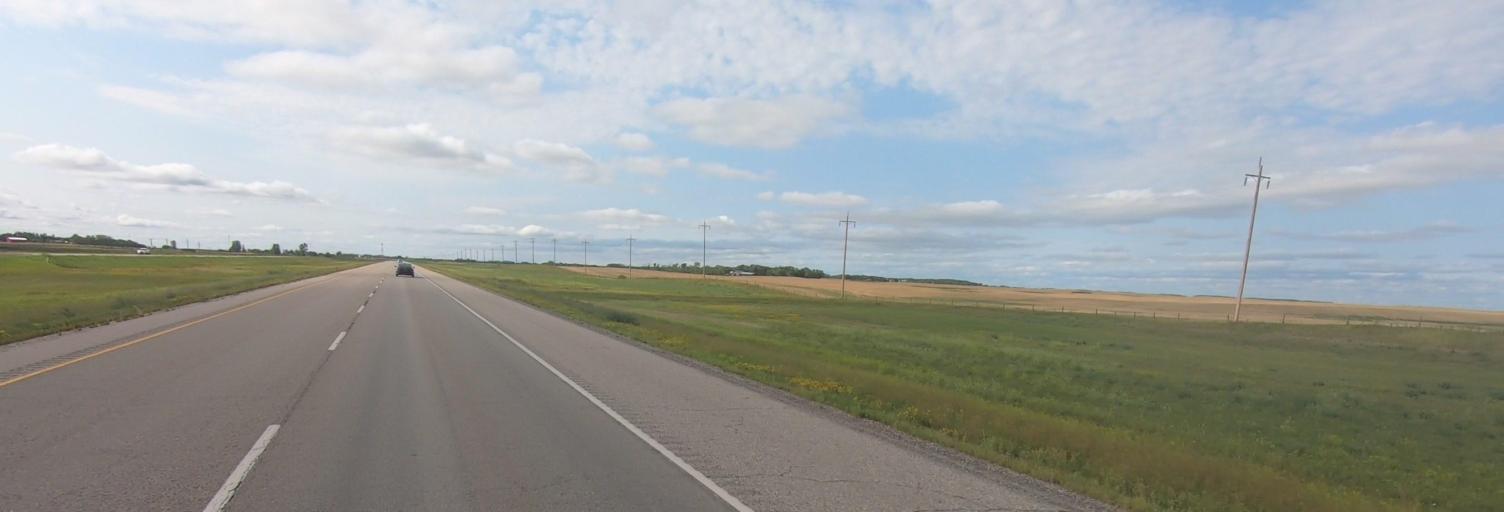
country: CA
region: Manitoba
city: Virden
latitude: 49.9256
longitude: -101.0947
